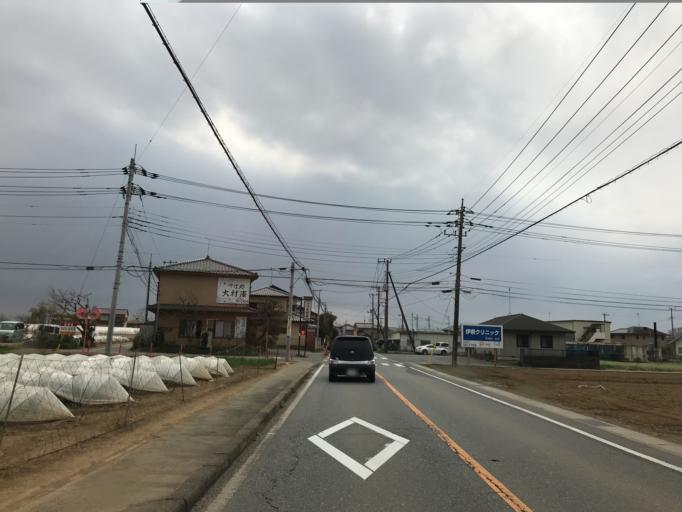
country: JP
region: Ibaraki
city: Moriya
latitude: 35.9856
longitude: 140.0575
